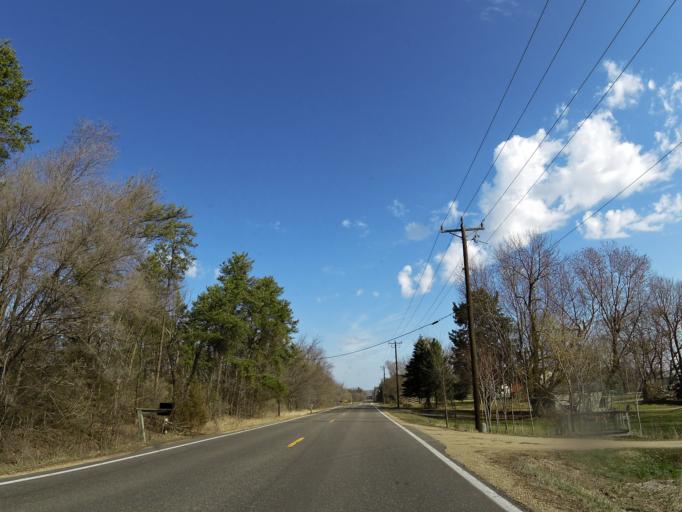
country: US
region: Minnesota
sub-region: Washington County
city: Afton
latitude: 44.9280
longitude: -92.8428
